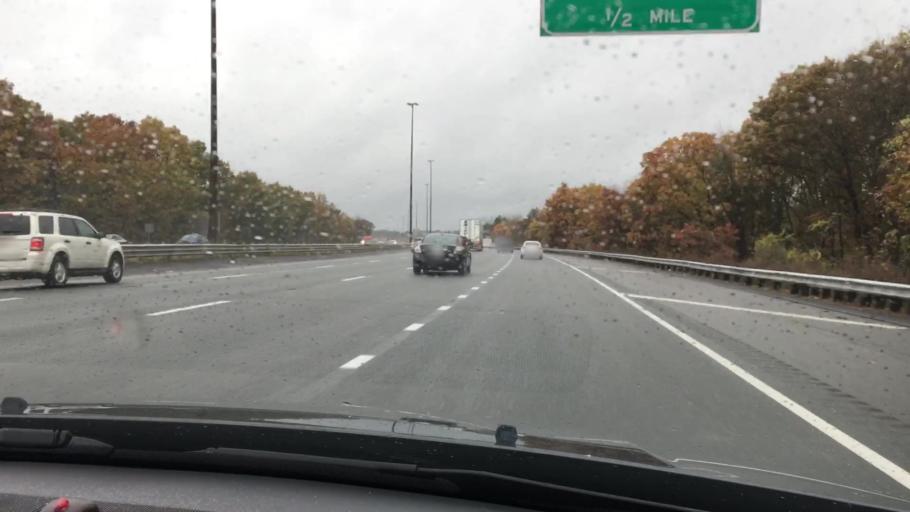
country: US
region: Massachusetts
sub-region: Middlesex County
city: Chelmsford
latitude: 42.6071
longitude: -71.3362
